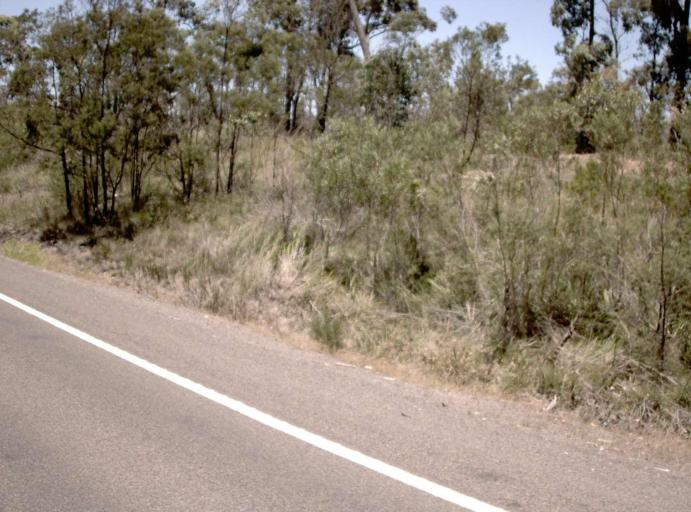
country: AU
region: Victoria
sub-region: East Gippsland
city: Lakes Entrance
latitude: -37.7524
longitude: 148.2082
